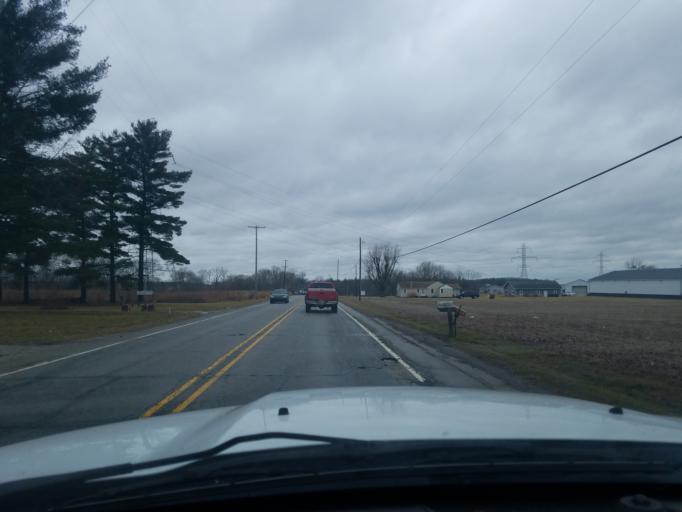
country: US
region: Indiana
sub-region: Noble County
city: Rome City
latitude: 41.4530
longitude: -85.3838
